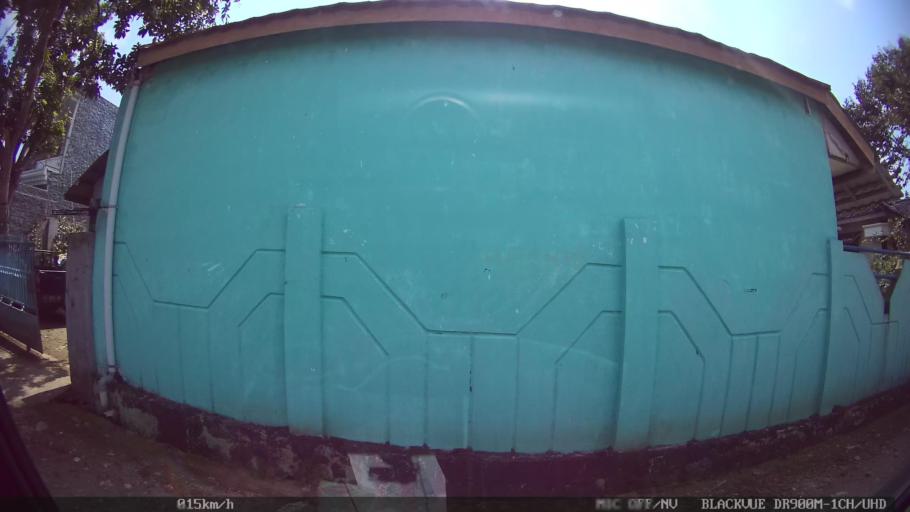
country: ID
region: Lampung
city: Kedaton
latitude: -5.3579
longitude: 105.2847
